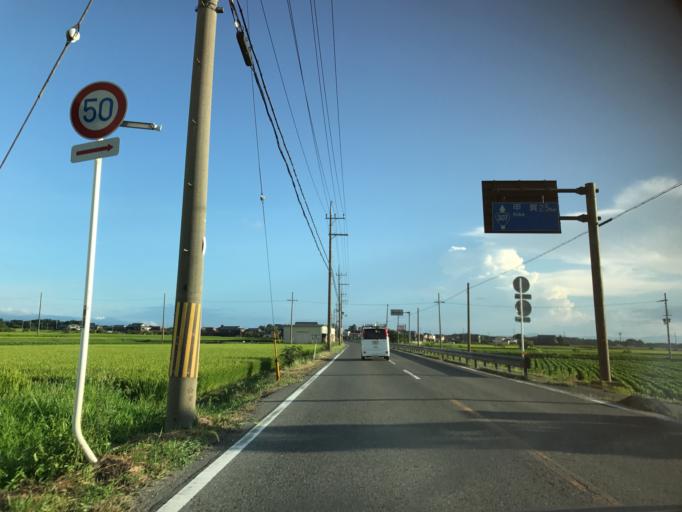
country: JP
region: Shiga Prefecture
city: Youkaichi
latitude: 35.1343
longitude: 136.2618
